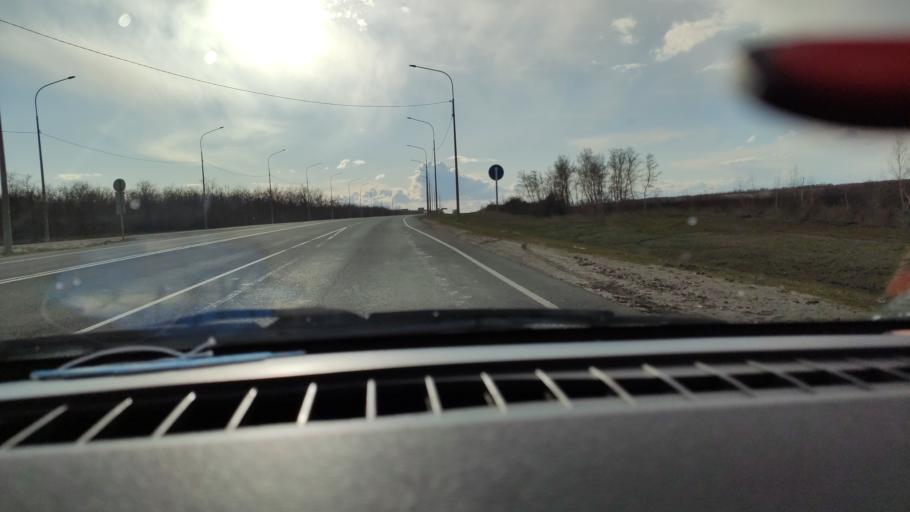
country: RU
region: Saratov
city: Yelshanka
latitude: 51.8201
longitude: 46.3493
